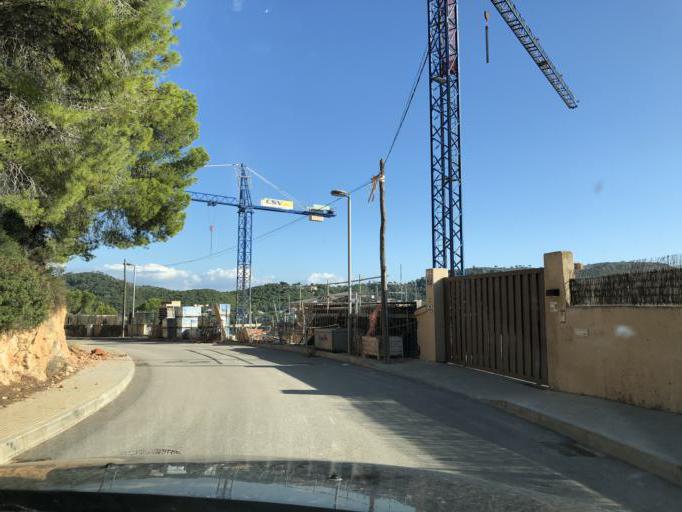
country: ES
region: Balearic Islands
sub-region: Illes Balears
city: Camp de Mar
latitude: 39.5397
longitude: 2.4116
